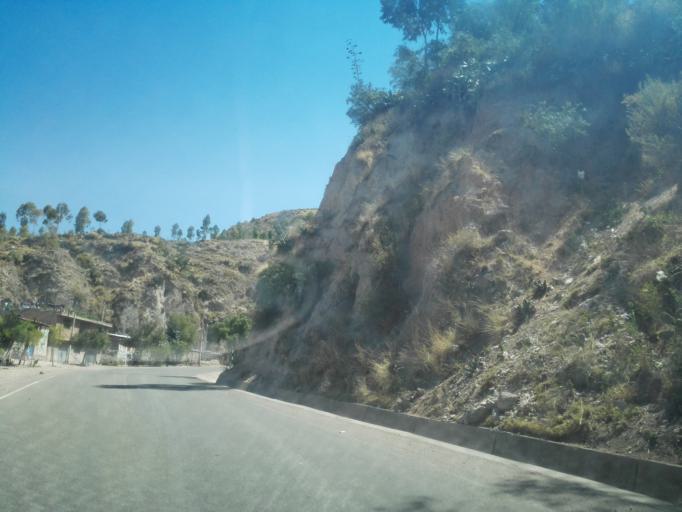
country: PE
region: Ayacucho
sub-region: Provincia de Huamanga
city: Ayacucho
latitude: -13.1582
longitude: -74.2372
